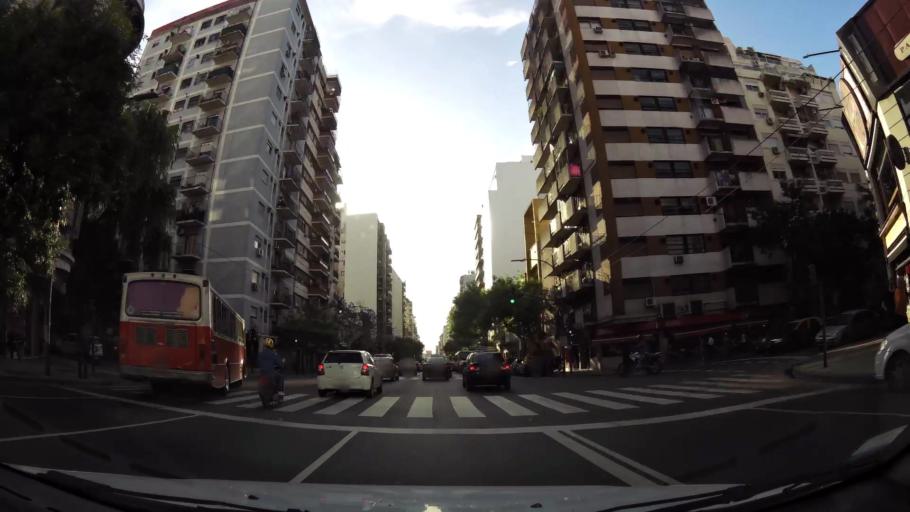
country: AR
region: Buenos Aires F.D.
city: Retiro
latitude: -34.5980
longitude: -58.4131
